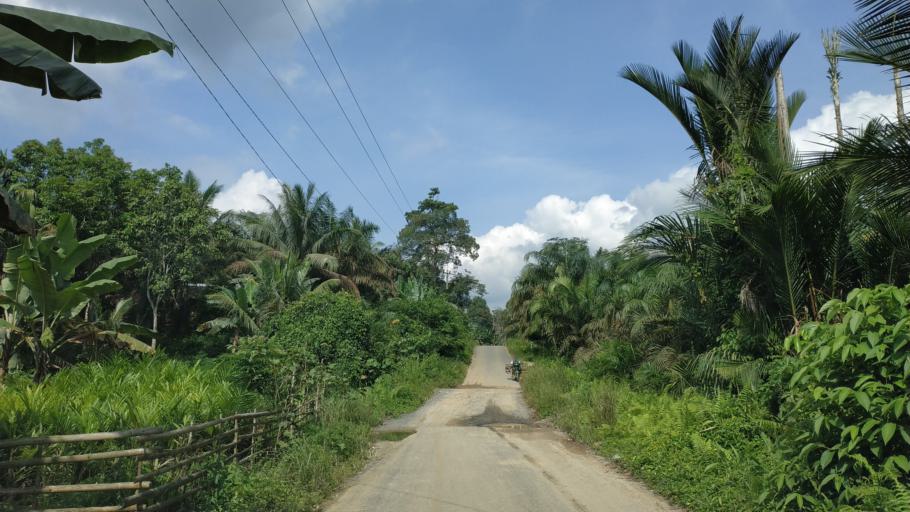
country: ID
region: Riau
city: Pangkalan Kasai
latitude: -0.7262
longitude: 102.4800
